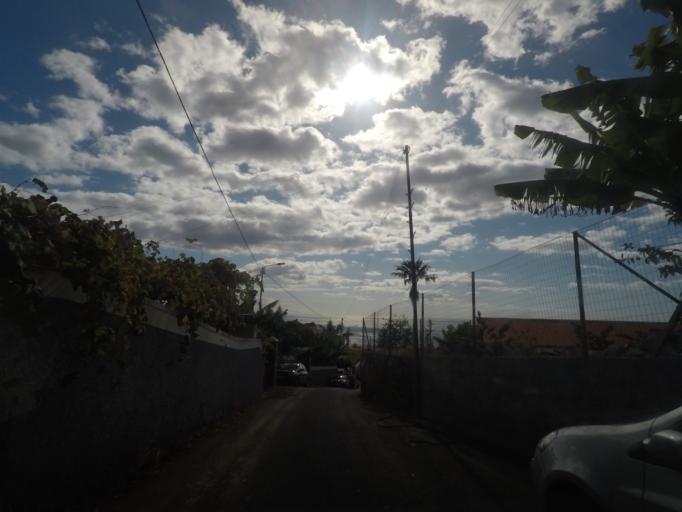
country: PT
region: Madeira
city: Camara de Lobos
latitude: 32.6585
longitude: -16.9542
